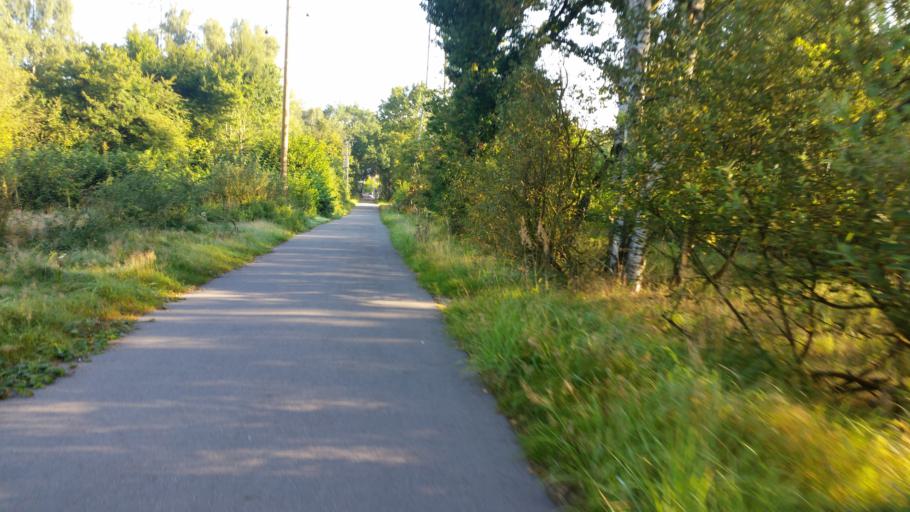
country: DE
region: Lower Saxony
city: Tappenbeck
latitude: 52.4331
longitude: 10.7419
